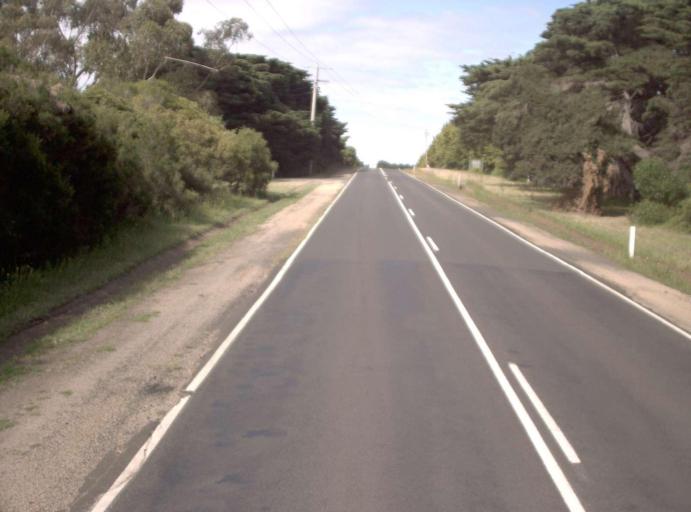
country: AU
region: Victoria
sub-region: Bass Coast
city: Phillip Island
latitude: -38.4818
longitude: 145.1766
